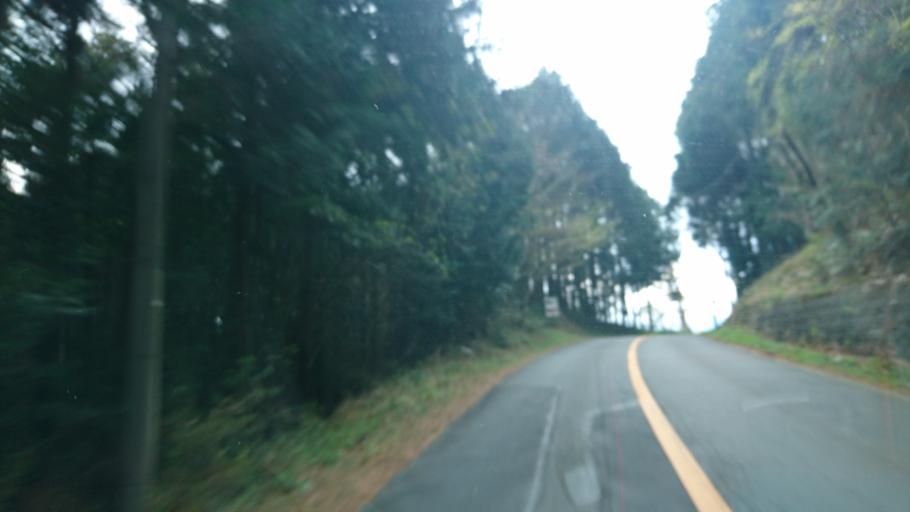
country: JP
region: Shizuoka
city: Fujinomiya
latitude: 35.2678
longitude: 138.5848
